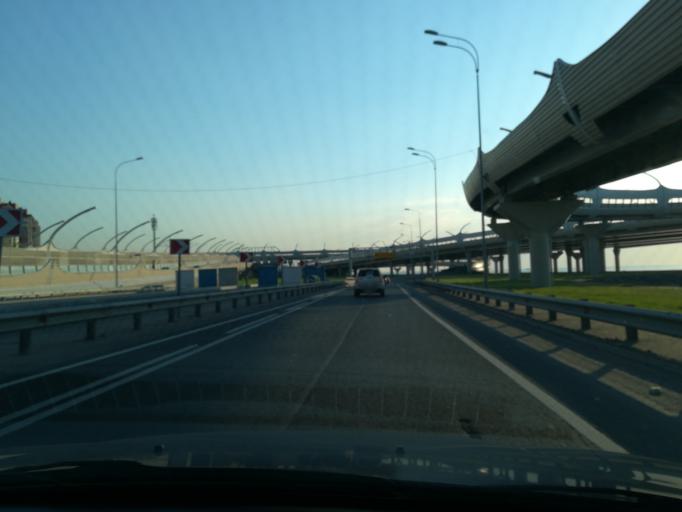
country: RU
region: St.-Petersburg
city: Staraya Derevnya
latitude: 59.9611
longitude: 30.2195
